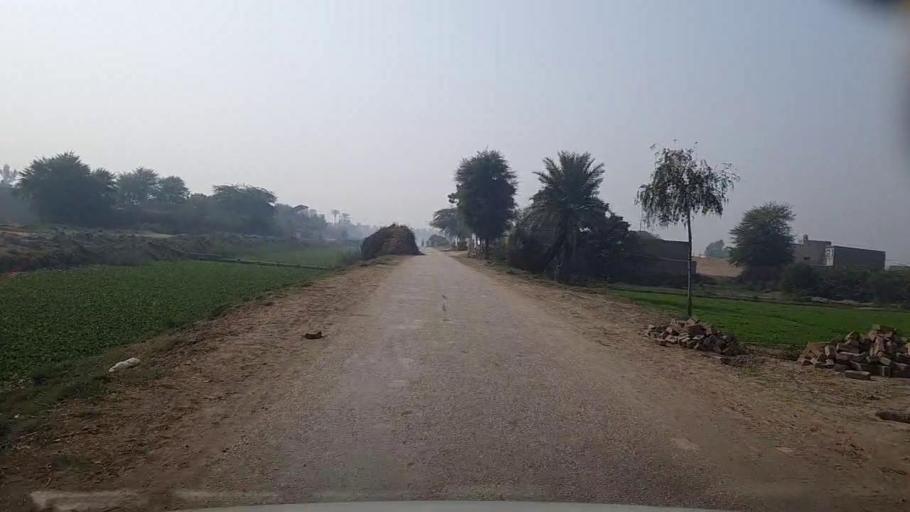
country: PK
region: Sindh
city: Setharja Old
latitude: 27.1955
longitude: 68.4797
